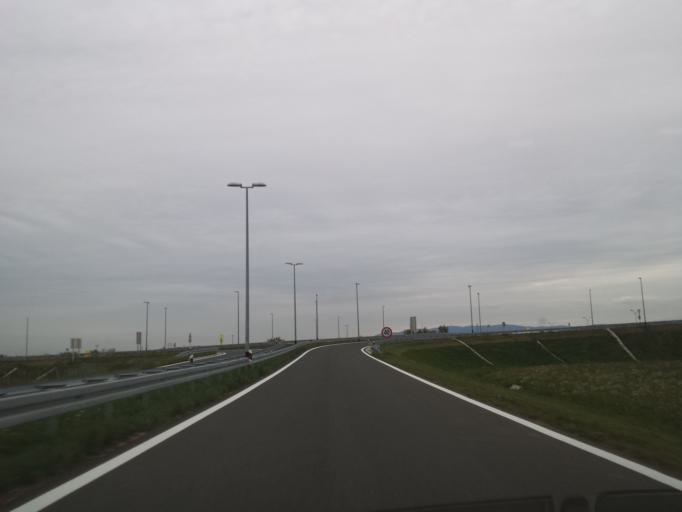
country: HR
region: Grad Zagreb
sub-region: Sesvete
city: Sesvete
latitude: 45.7907
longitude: 16.1655
